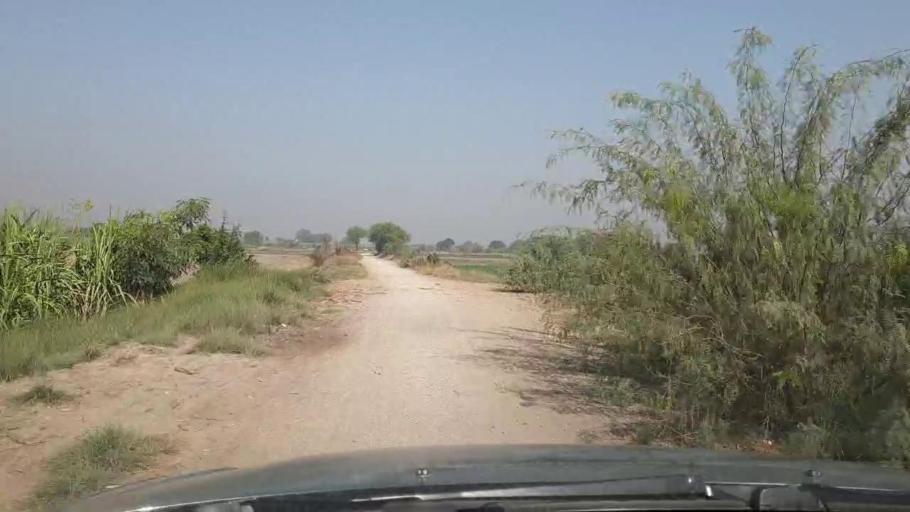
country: PK
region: Sindh
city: Tando Jam
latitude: 25.2841
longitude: 68.5336
